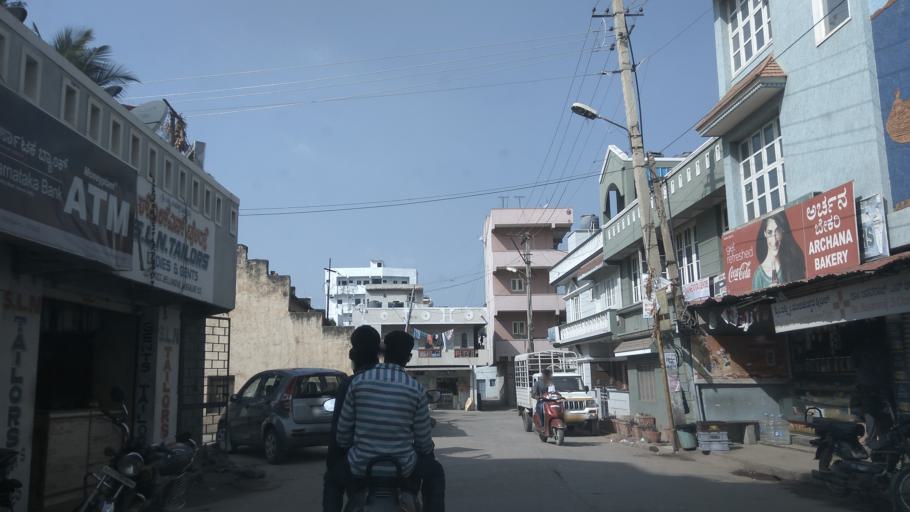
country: IN
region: Karnataka
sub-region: Bangalore Urban
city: Bangalore
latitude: 12.9300
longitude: 77.6766
